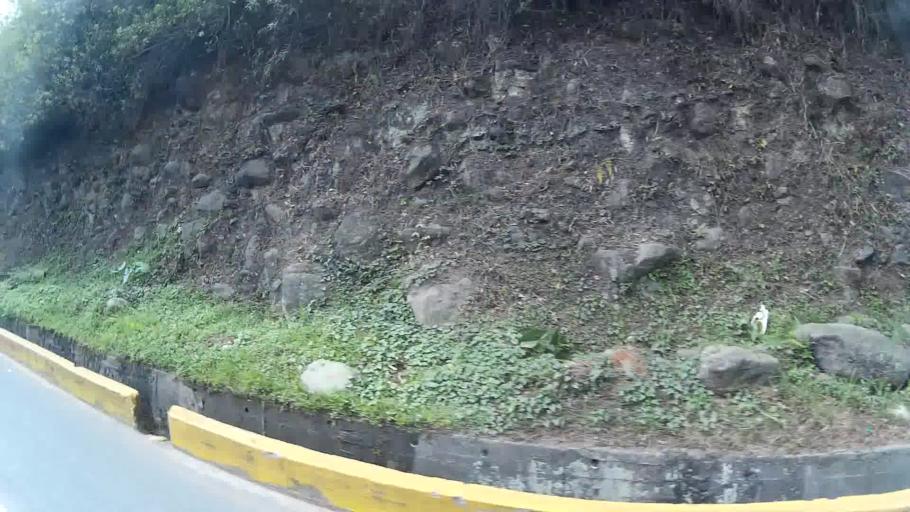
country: CO
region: Risaralda
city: Pereira
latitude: 4.8191
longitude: -75.7397
